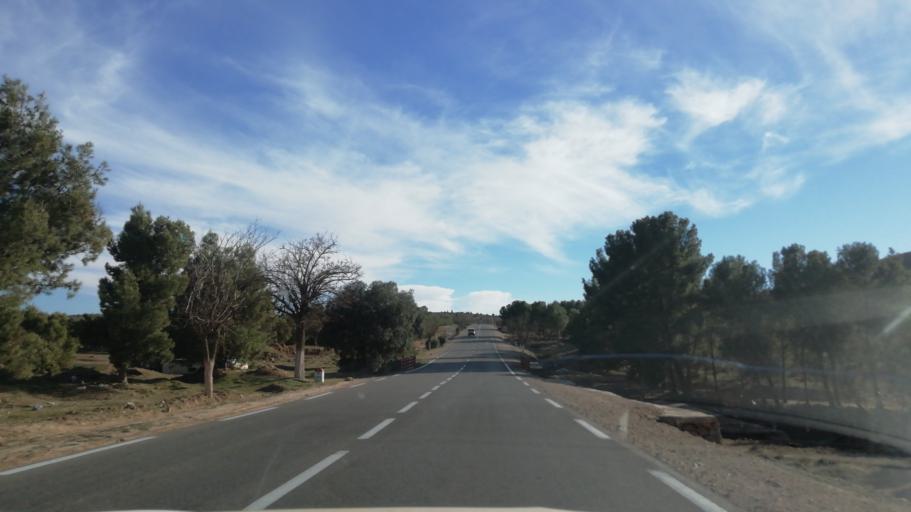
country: DZ
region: Tlemcen
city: Sebdou
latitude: 34.5907
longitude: -1.3185
